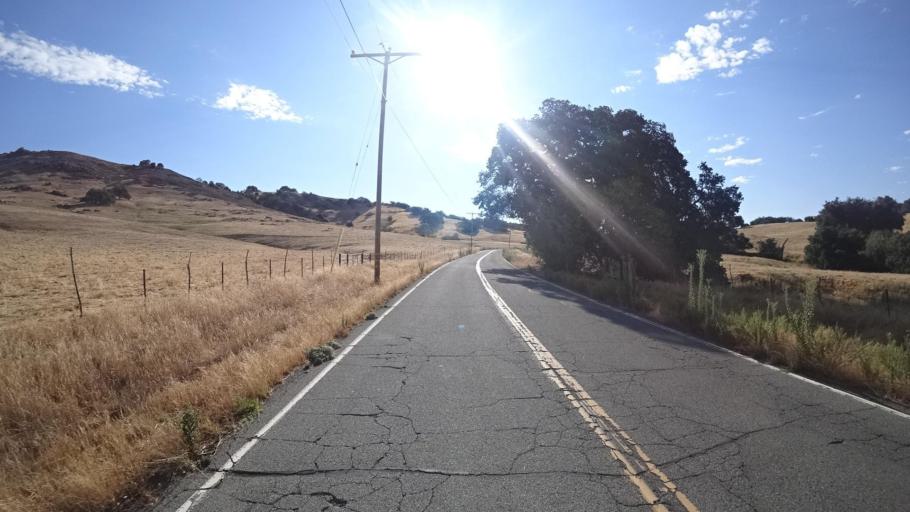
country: US
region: California
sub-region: San Diego County
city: Julian
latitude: 33.1593
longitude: -116.7199
